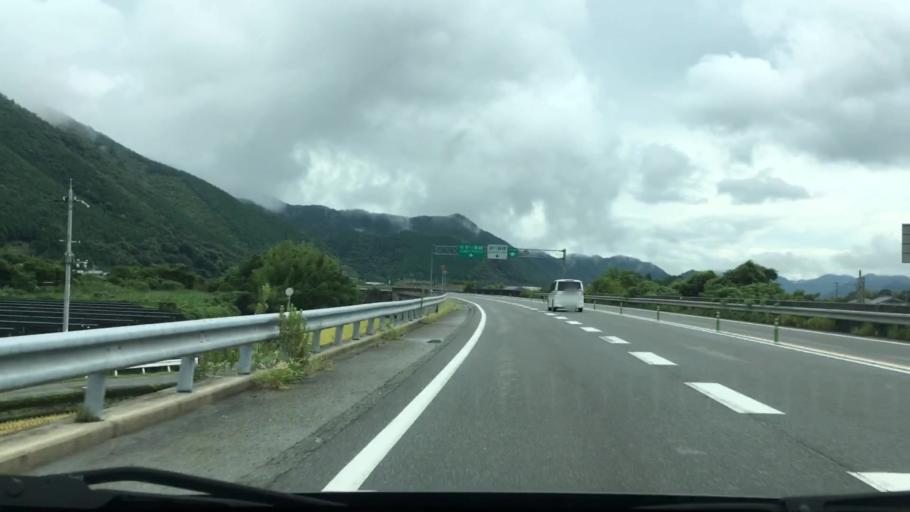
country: JP
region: Hyogo
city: Yamazakicho-nakabirose
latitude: 35.0505
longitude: 134.7640
